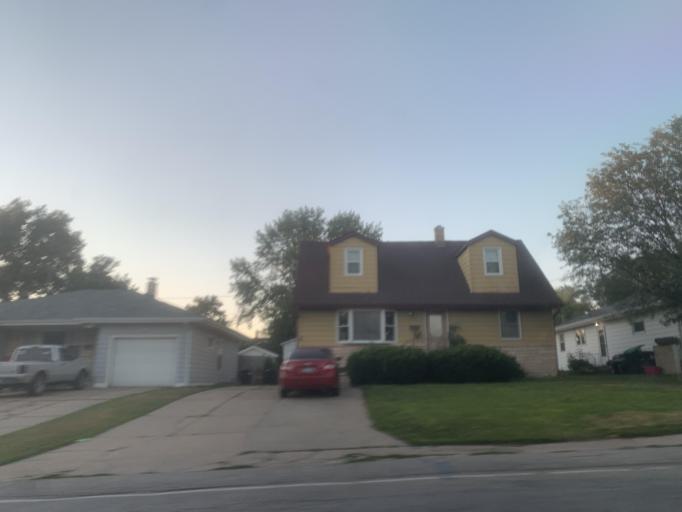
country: US
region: Nebraska
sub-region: Sarpy County
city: La Vista
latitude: 41.2053
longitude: -95.9973
